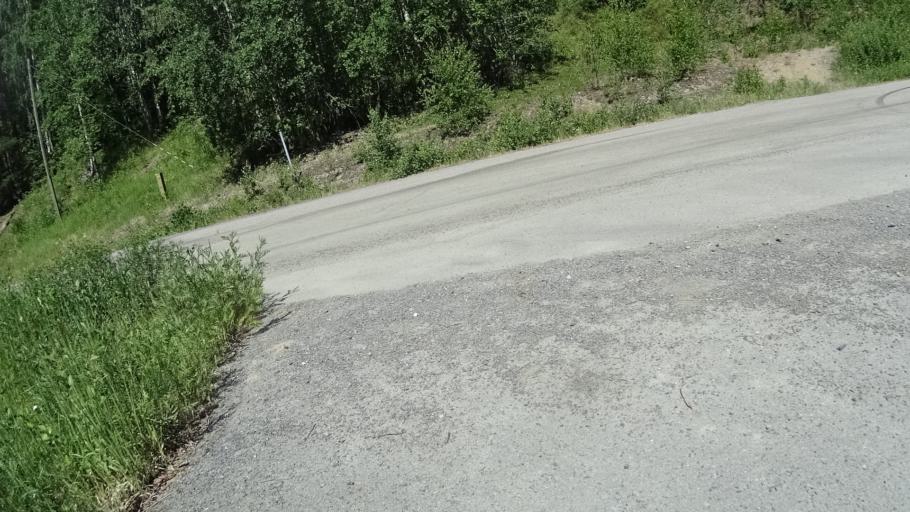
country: FI
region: Uusimaa
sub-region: Raaseporin
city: Pohja
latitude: 60.0945
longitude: 23.5712
